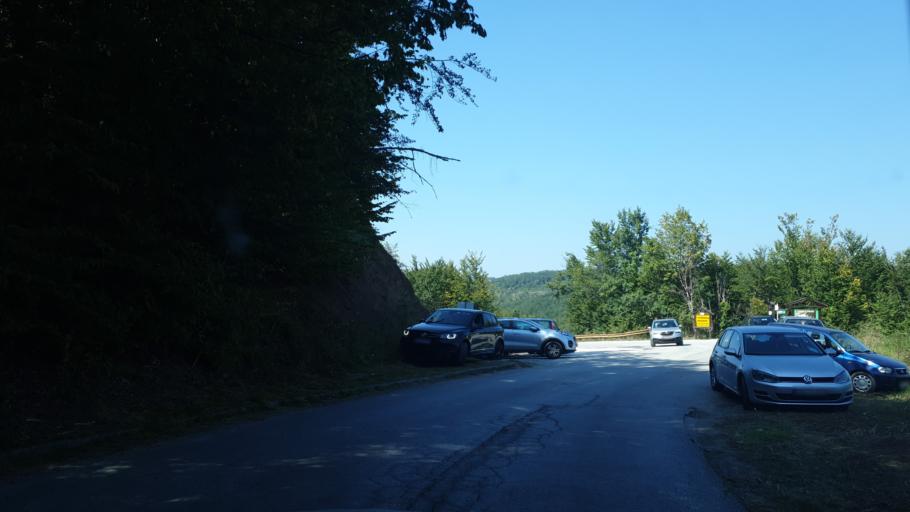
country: RS
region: Central Serbia
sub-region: Zlatiborski Okrug
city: Cajetina
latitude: 43.7021
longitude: 19.8470
